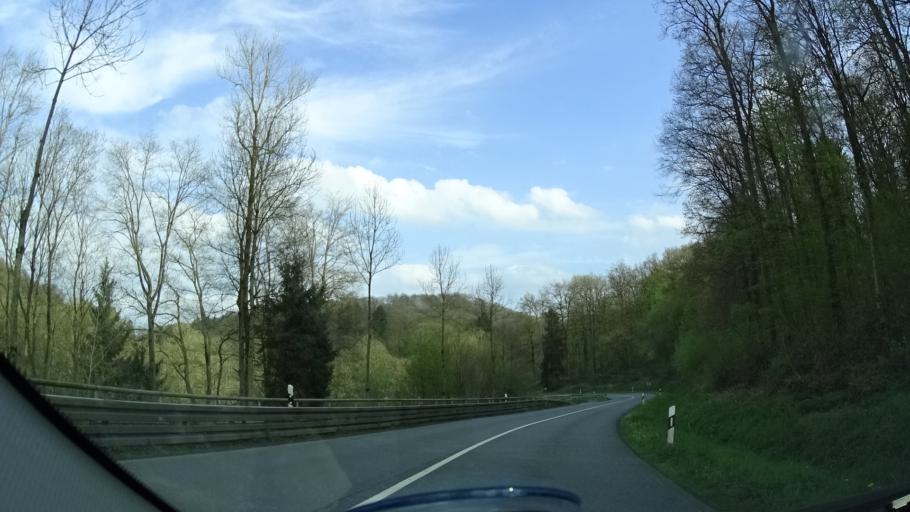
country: DE
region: North Rhine-Westphalia
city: Warstein
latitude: 51.4654
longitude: 8.3901
